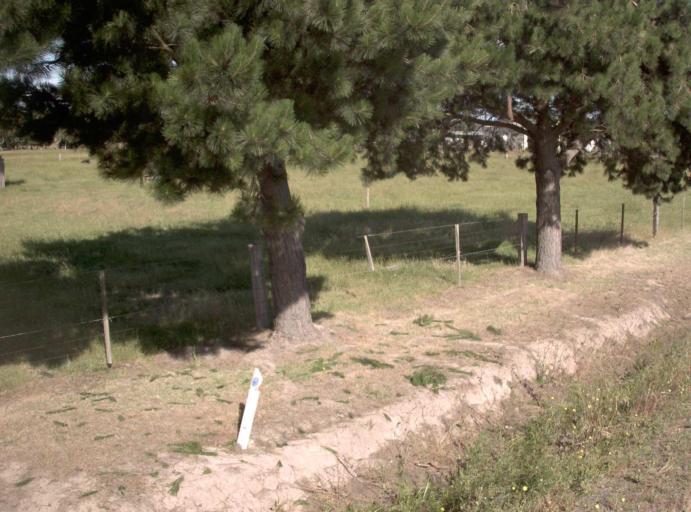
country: AU
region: Victoria
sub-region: Latrobe
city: Traralgon
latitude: -38.1846
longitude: 146.5018
